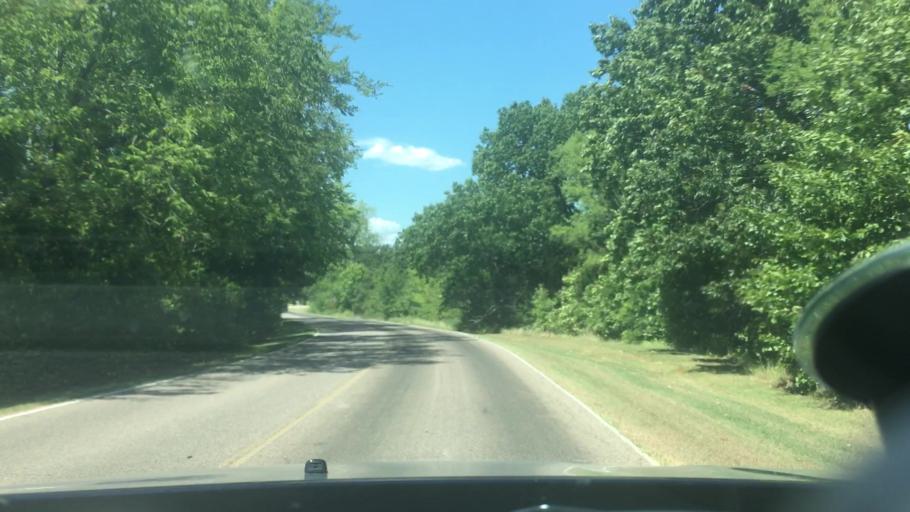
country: US
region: Oklahoma
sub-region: Marshall County
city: Kingston
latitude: 33.9856
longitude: -96.6367
